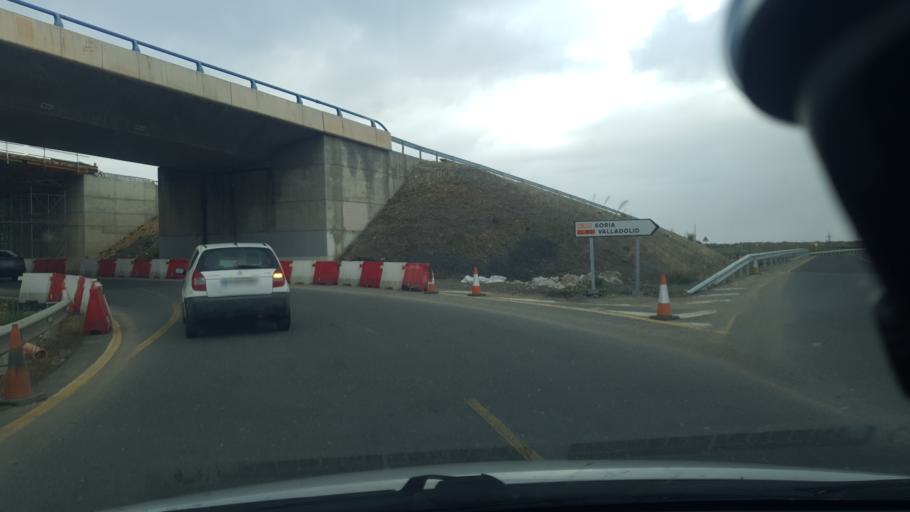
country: ES
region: Castille and Leon
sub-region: Provincia de Segovia
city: Palazuelos de Eresma
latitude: 40.9276
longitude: -4.0863
